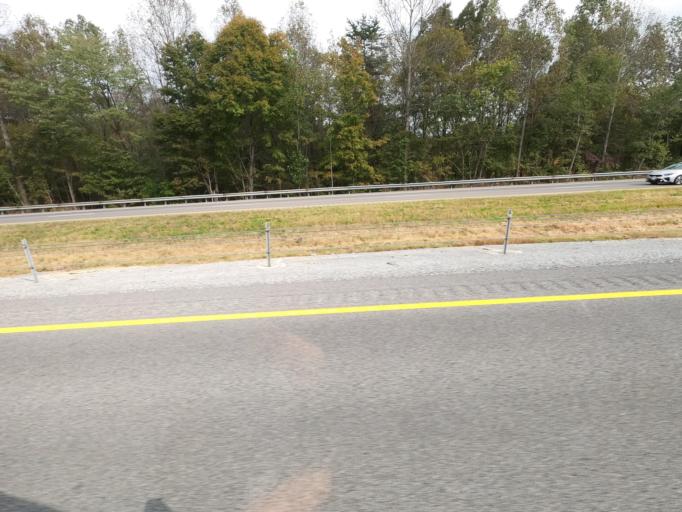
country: US
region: Tennessee
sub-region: Williamson County
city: Fairview
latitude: 36.0252
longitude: -87.1939
